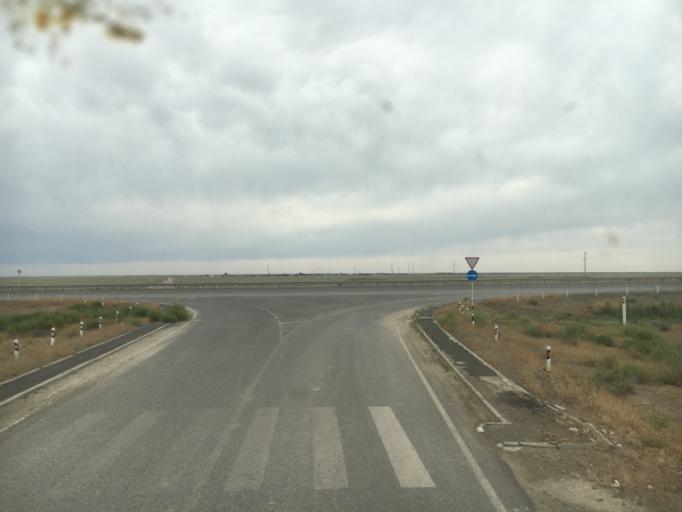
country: KZ
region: Qyzylorda
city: Shalqiya
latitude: 43.6068
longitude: 67.6715
